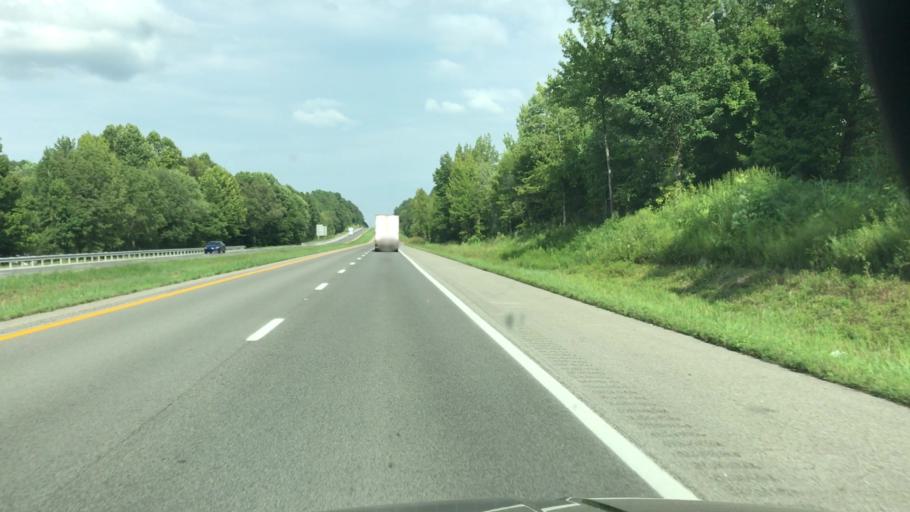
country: US
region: Kentucky
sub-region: Muhlenberg County
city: Morehead
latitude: 37.2482
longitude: -87.2333
